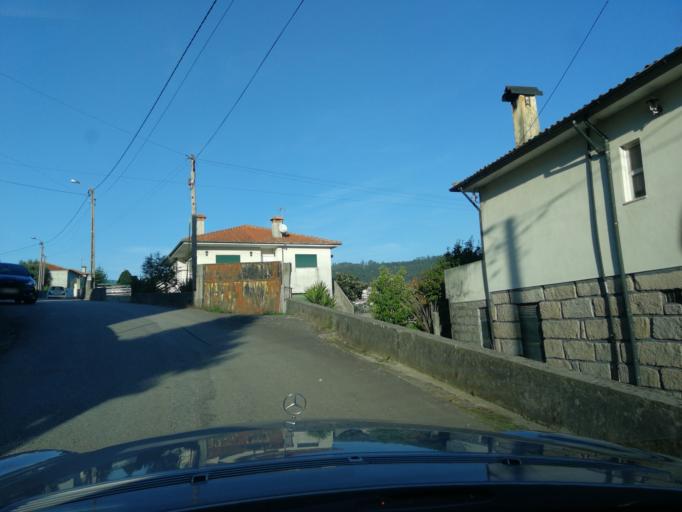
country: PT
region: Braga
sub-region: Braga
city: Oliveira
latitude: 41.4570
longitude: -8.4542
